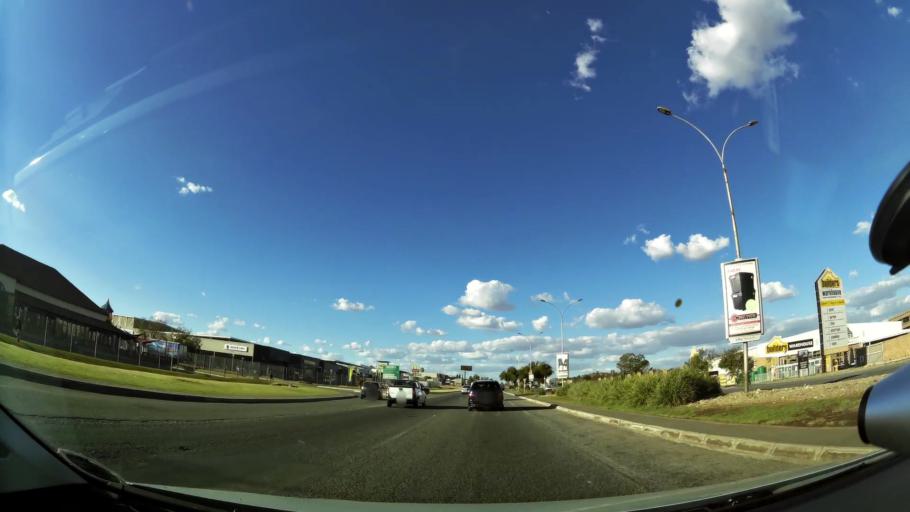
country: ZA
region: North-West
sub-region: Dr Kenneth Kaunda District Municipality
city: Klerksdorp
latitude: -26.8568
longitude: 26.6753
